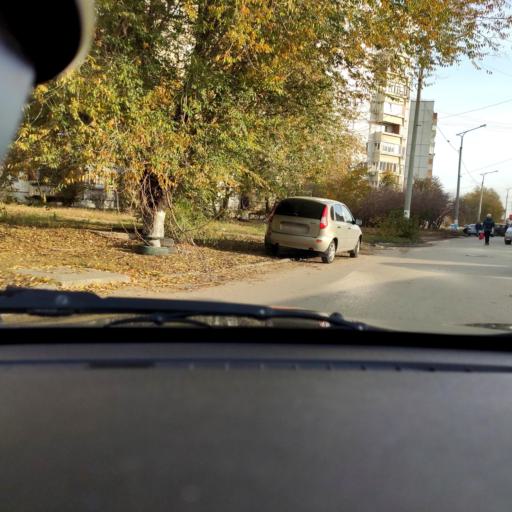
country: RU
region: Samara
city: Tol'yatti
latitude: 53.5399
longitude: 49.4002
